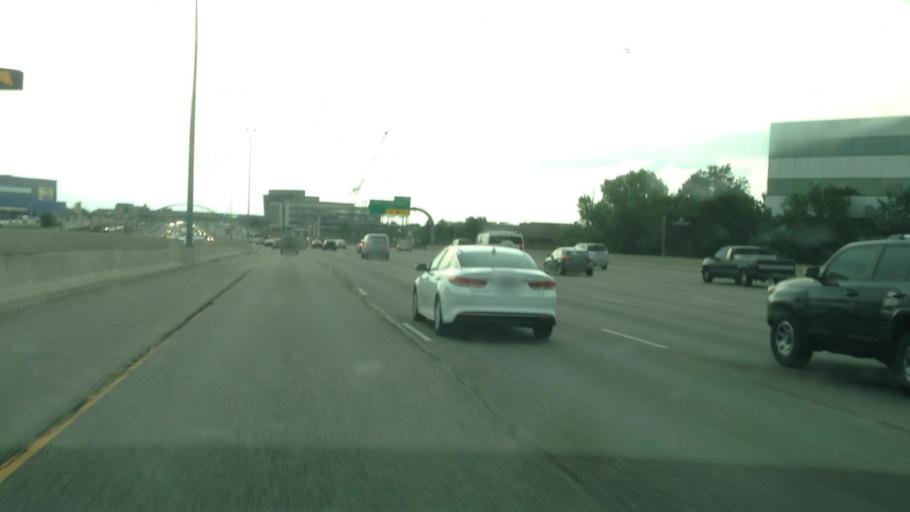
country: US
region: Colorado
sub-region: Arapahoe County
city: Centennial
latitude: 39.5703
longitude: -104.8726
